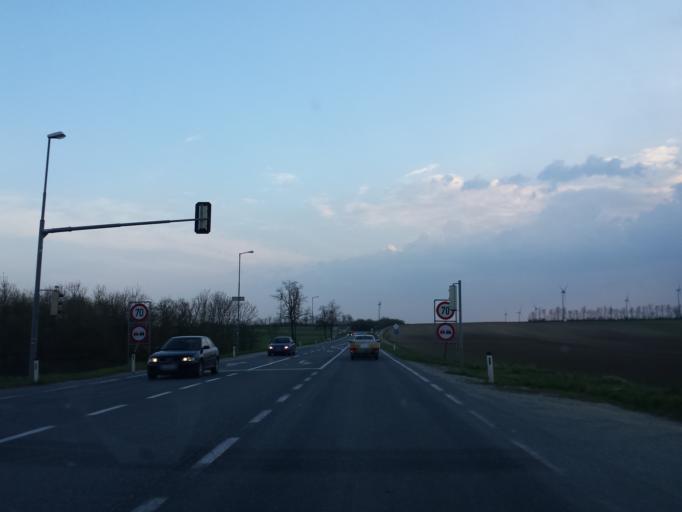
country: AT
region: Lower Austria
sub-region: Politischer Bezirk Mistelbach
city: Wilfersdorf
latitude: 48.5620
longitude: 16.6366
